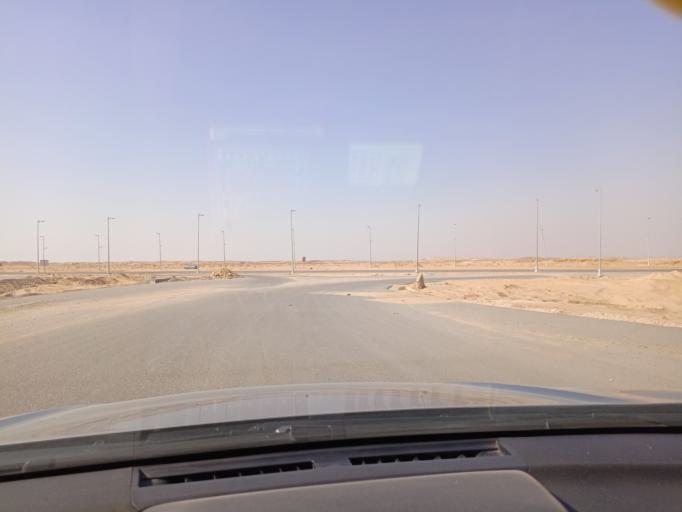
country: EG
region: Muhafazat al Qalyubiyah
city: Al Khankah
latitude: 30.0431
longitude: 31.7132
